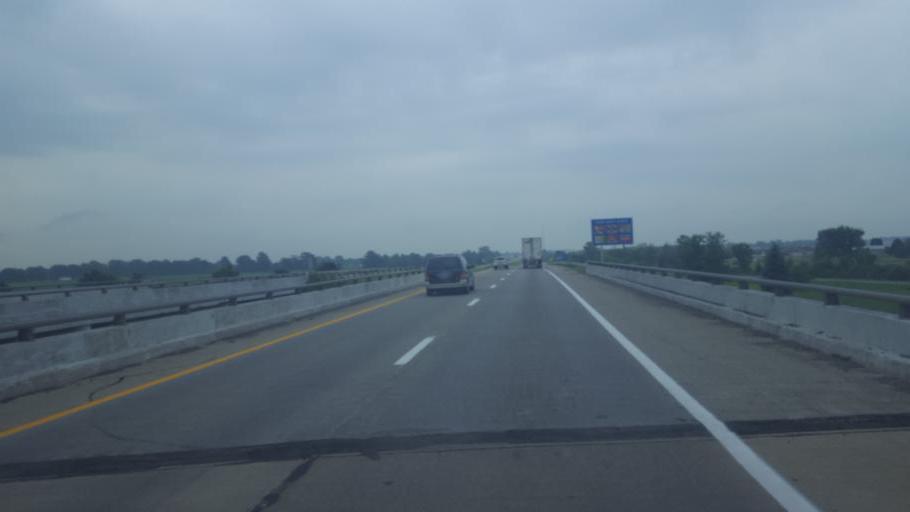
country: US
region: Ohio
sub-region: Marion County
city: Marion
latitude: 40.5949
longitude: -83.0840
